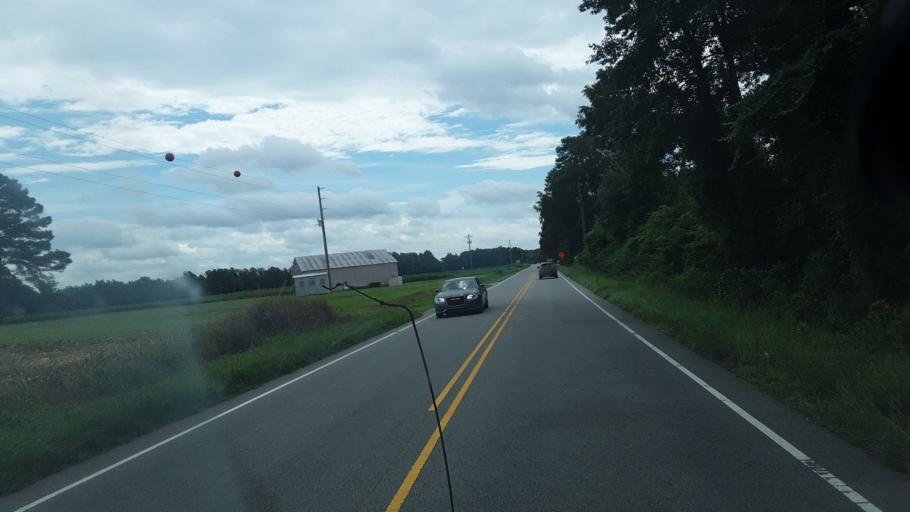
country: US
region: North Carolina
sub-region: Robeson County
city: Rowland
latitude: 34.5968
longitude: -79.3274
